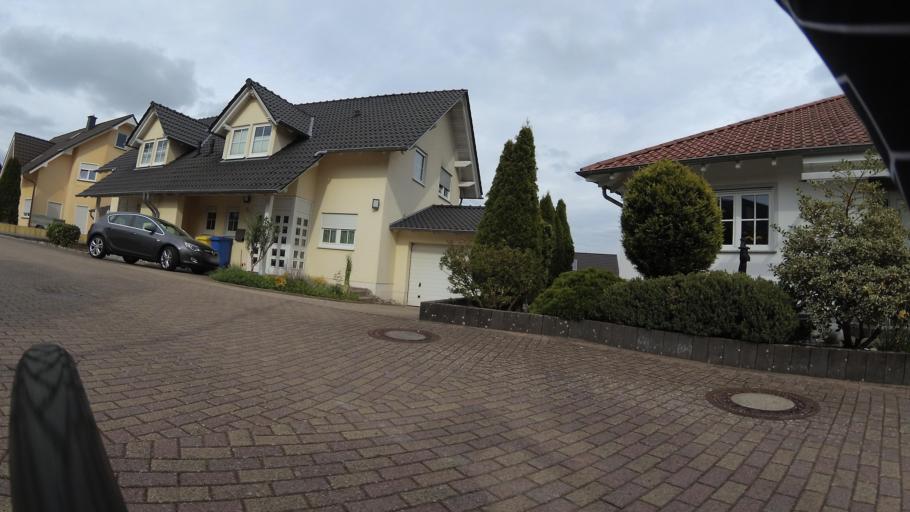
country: DE
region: Rheinland-Pfalz
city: Zweibrucken
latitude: 49.2364
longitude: 7.3518
